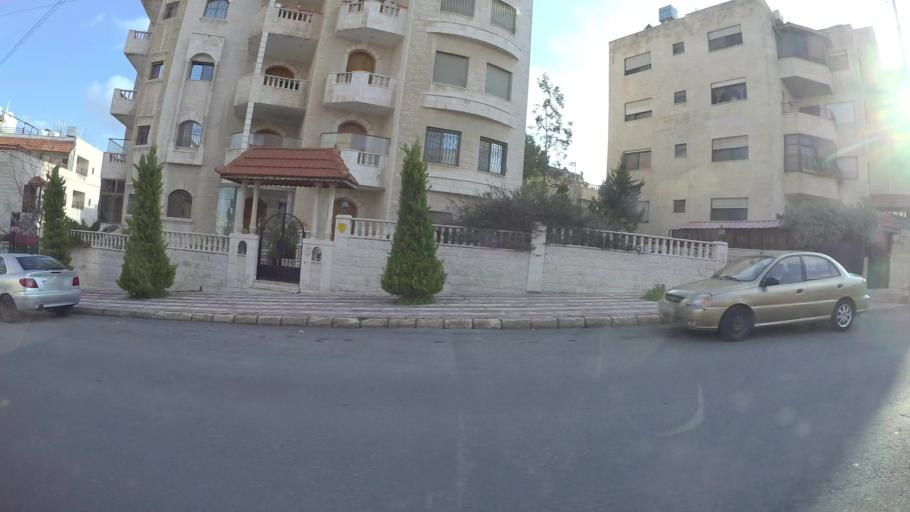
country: JO
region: Amman
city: Al Jubayhah
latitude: 31.9808
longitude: 35.8557
